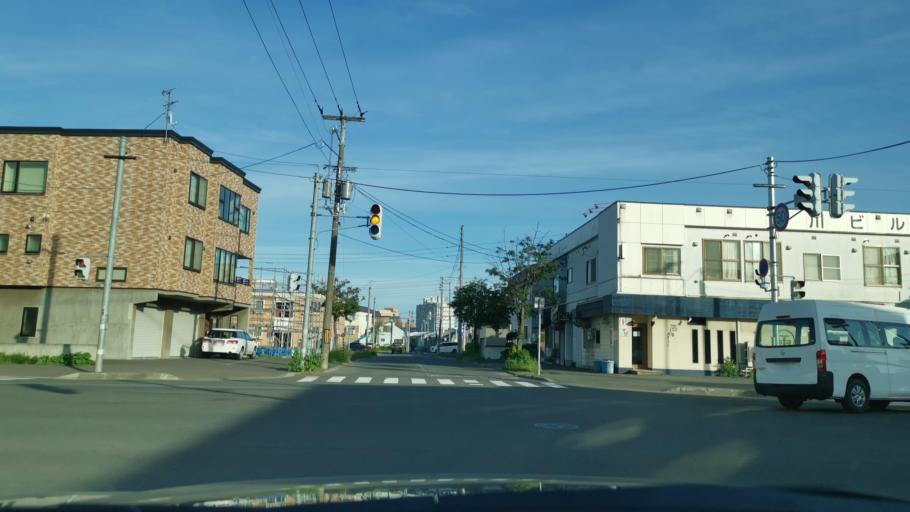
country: JP
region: Hokkaido
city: Sapporo
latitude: 43.0697
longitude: 141.4035
